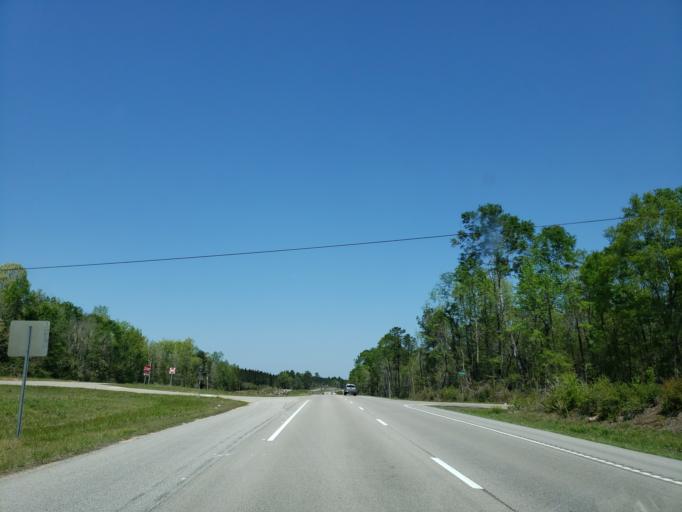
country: US
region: Mississippi
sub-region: Stone County
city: Wiggins
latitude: 30.9756
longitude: -89.1980
